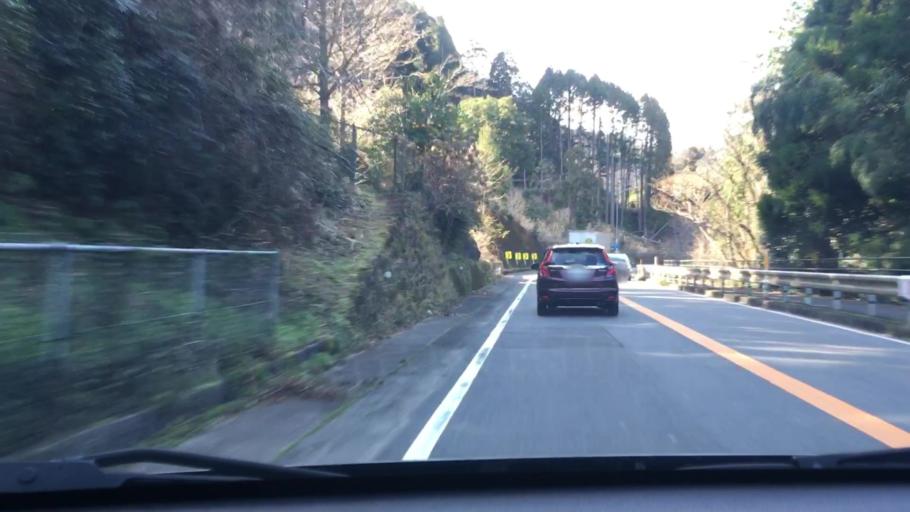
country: JP
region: Oita
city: Tsukumiura
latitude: 33.0005
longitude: 131.8107
